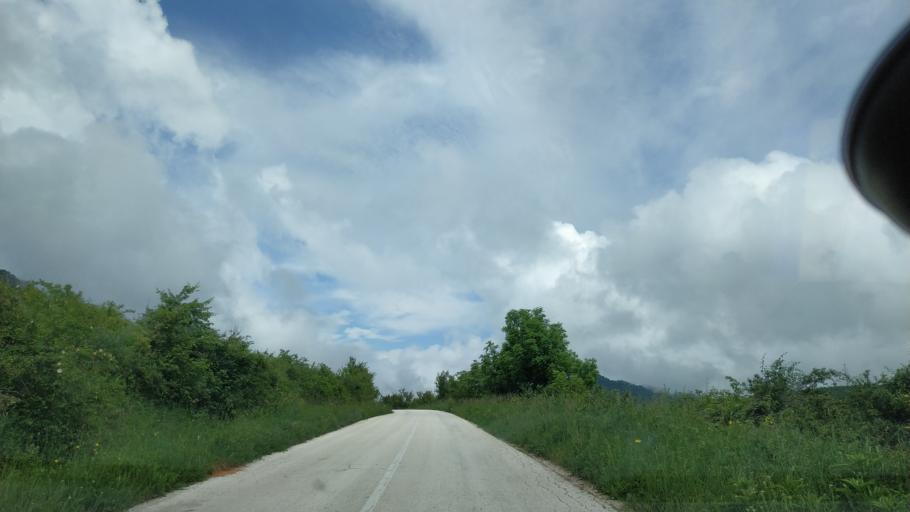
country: RS
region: Central Serbia
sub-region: Zajecarski Okrug
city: Boljevac
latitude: 43.7476
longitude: 21.9470
